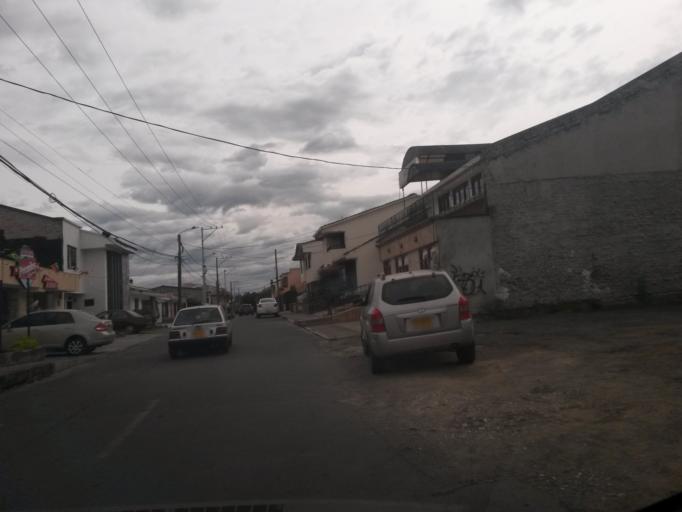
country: CO
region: Cauca
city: Popayan
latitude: 2.4571
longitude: -76.5976
